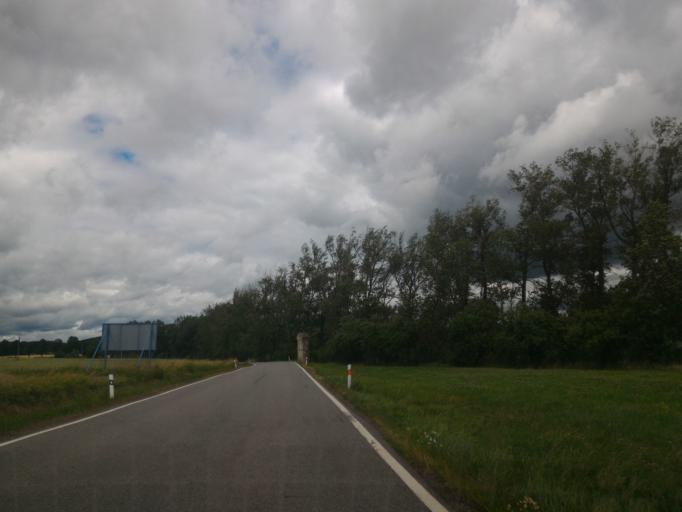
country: CZ
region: Vysocina
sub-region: Okres Jihlava
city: Telc
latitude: 49.1945
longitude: 15.4447
